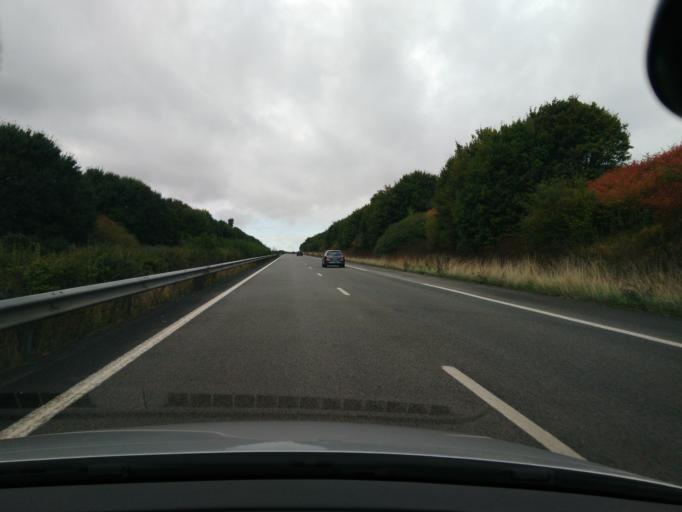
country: FR
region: Ile-de-France
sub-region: Departement des Yvelines
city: Houdan
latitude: 48.7824
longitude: 1.6046
